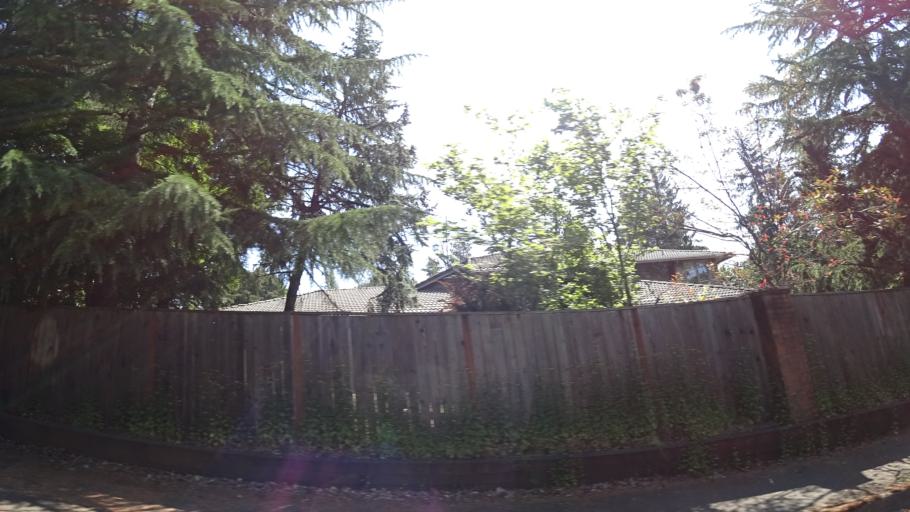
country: US
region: Oregon
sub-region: Washington County
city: Durham
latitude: 45.4209
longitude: -122.7221
